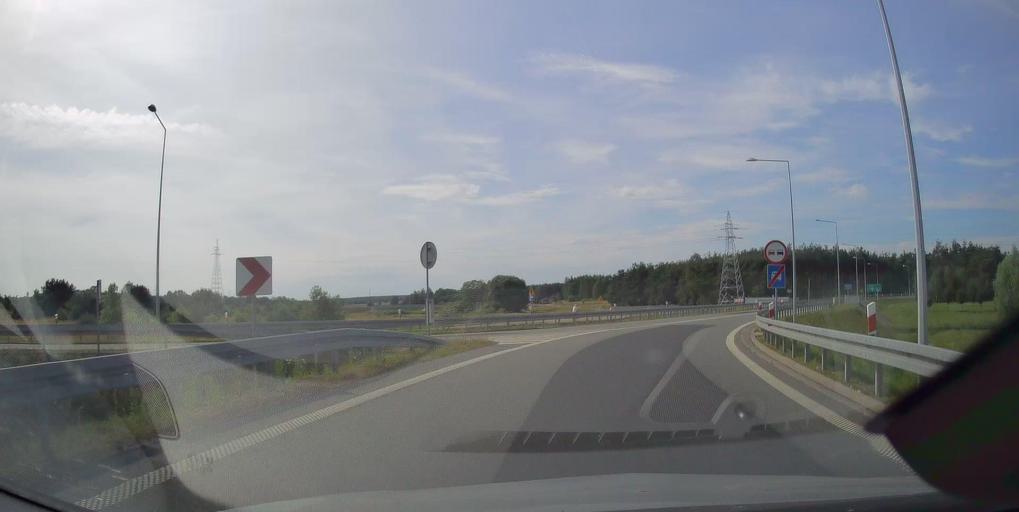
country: PL
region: Lodz Voivodeship
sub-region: Powiat tomaszowski
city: Tomaszow Mazowiecki
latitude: 51.5501
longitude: 19.9873
